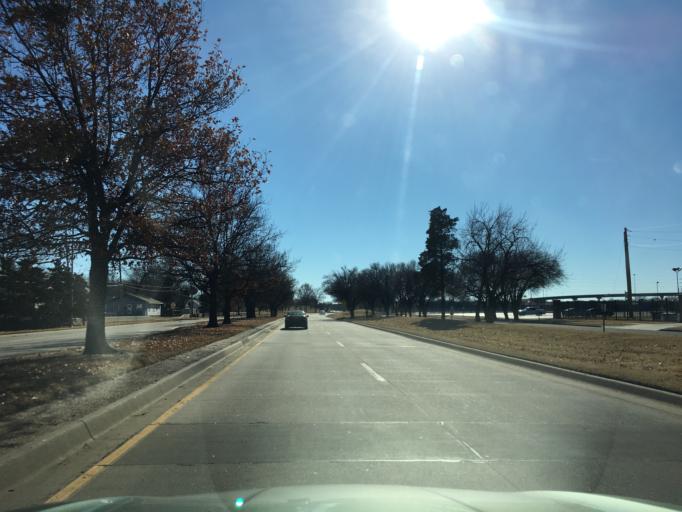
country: US
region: Kansas
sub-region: Sedgwick County
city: Wichita
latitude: 37.6838
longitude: -97.3078
